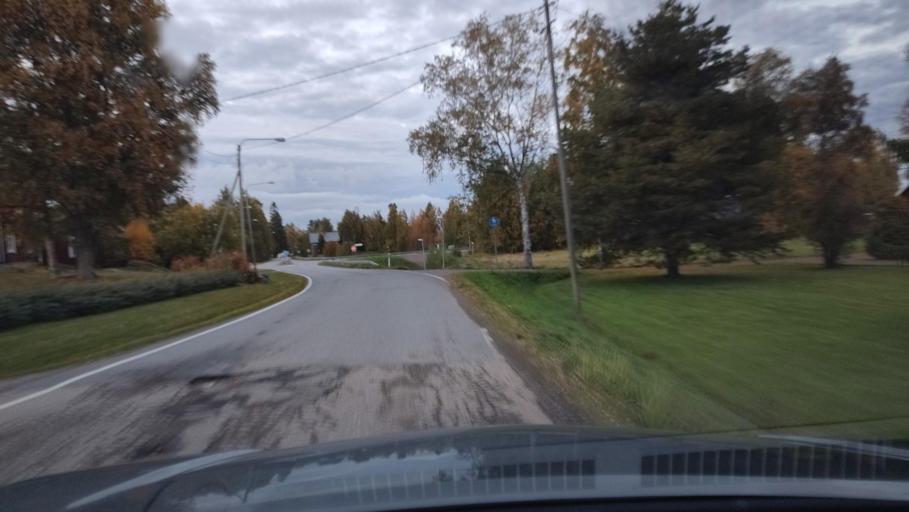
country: FI
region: Ostrobothnia
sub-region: Sydosterbotten
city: Kristinestad
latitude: 62.2595
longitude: 21.5080
